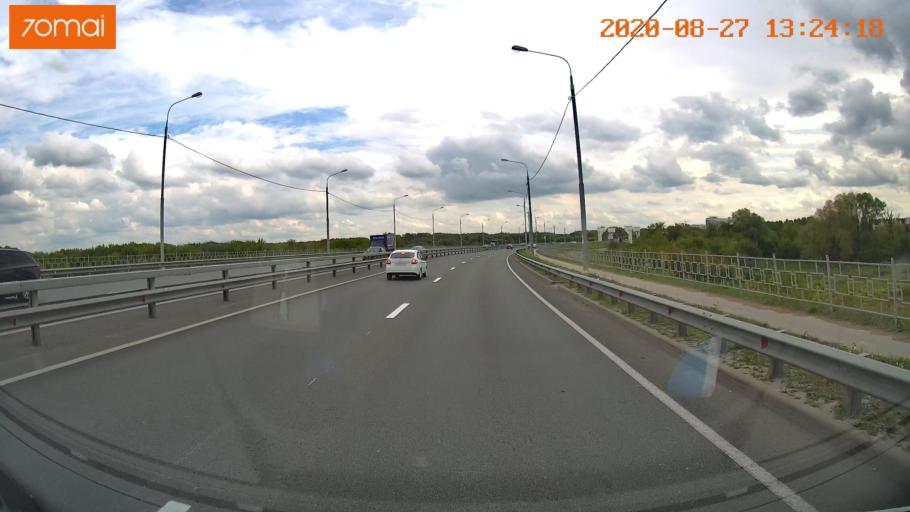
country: RU
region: Rjazan
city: Ryazan'
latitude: 54.6470
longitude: 39.7539
